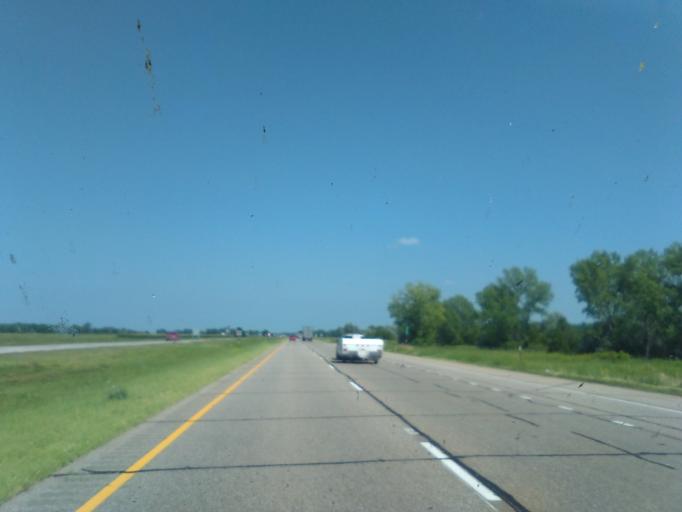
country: US
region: Nebraska
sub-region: Buffalo County
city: Kearney
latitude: 40.6753
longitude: -99.2503
